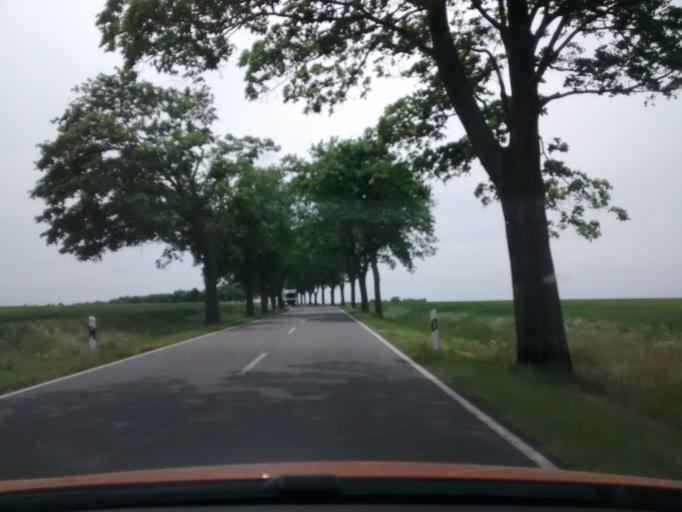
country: DE
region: Brandenburg
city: Juterbog
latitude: 51.9266
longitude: 13.1238
